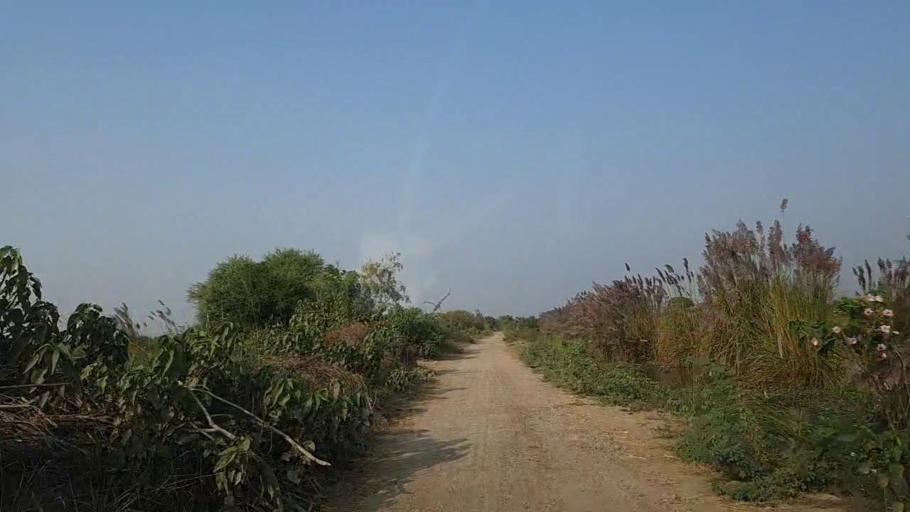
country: PK
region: Sindh
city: Mirpur Sakro
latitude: 24.6558
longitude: 67.7693
